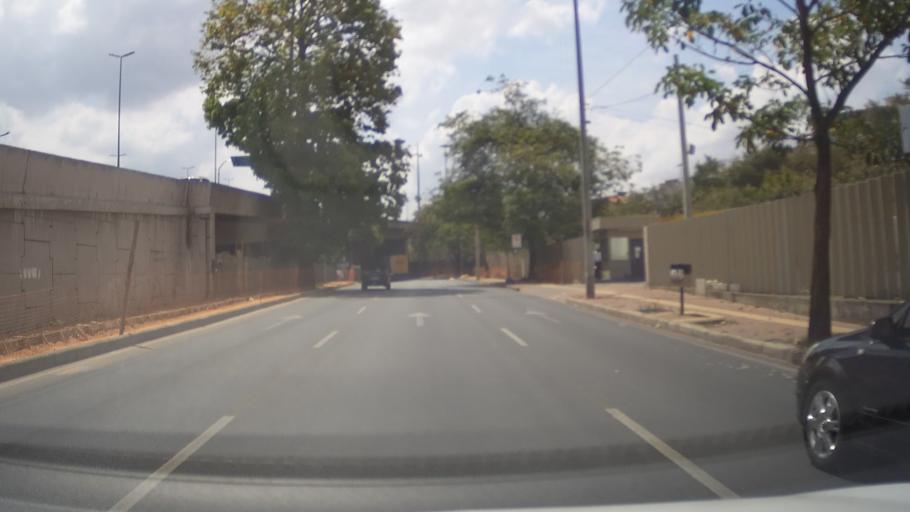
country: BR
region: Minas Gerais
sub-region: Belo Horizonte
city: Belo Horizonte
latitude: -19.9131
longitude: -43.9380
